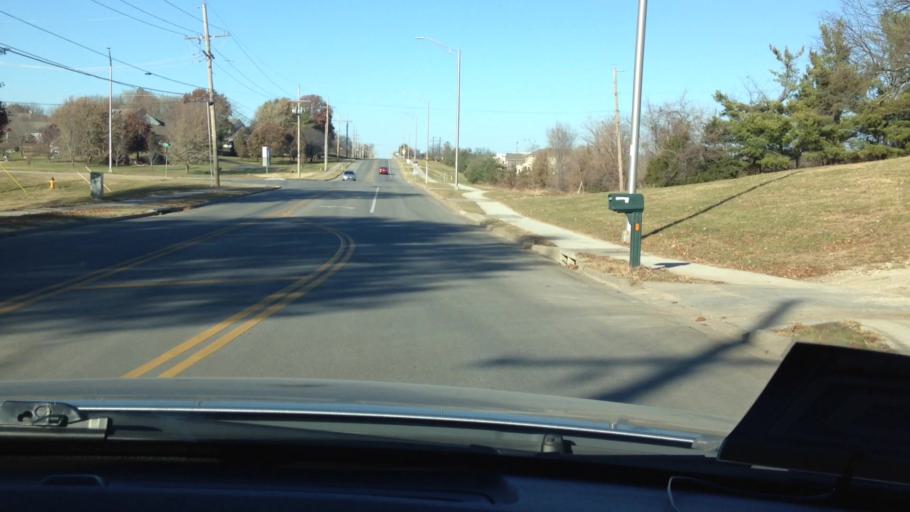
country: US
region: Kansas
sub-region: Johnson County
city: Olathe
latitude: 38.9120
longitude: -94.8160
